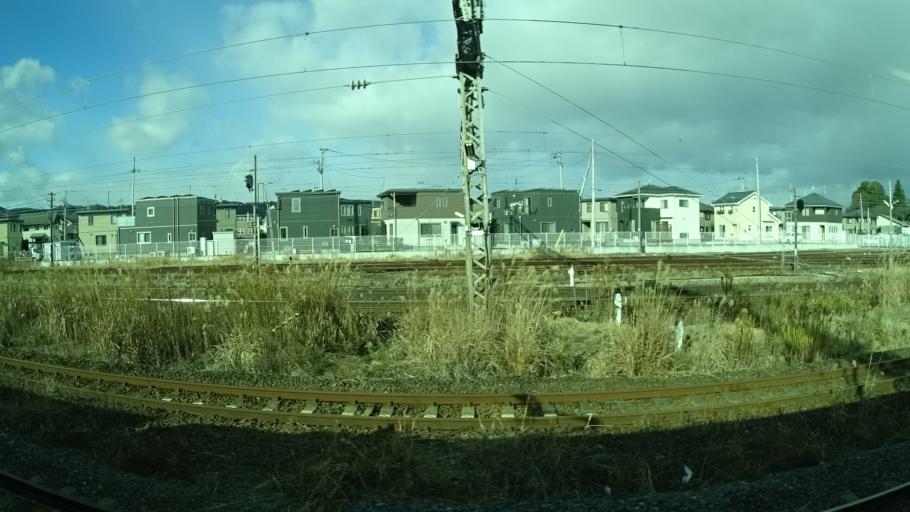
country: JP
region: Miyagi
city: Iwanuma
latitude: 38.1107
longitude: 140.8628
